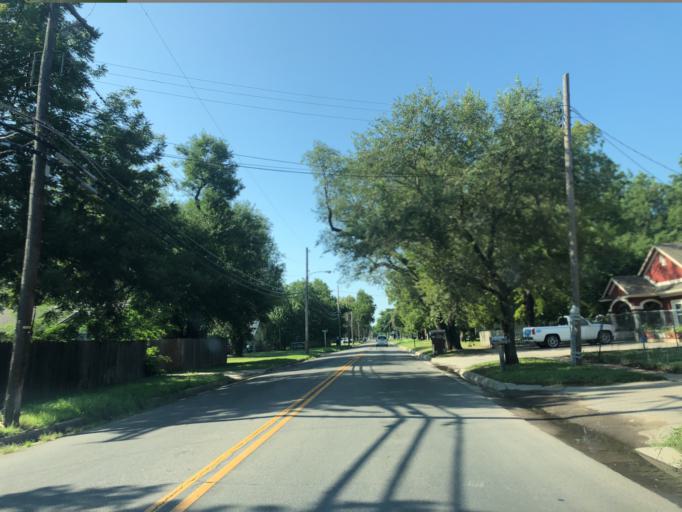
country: US
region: Kansas
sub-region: Sedgwick County
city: Wichita
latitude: 37.7349
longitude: -97.3448
